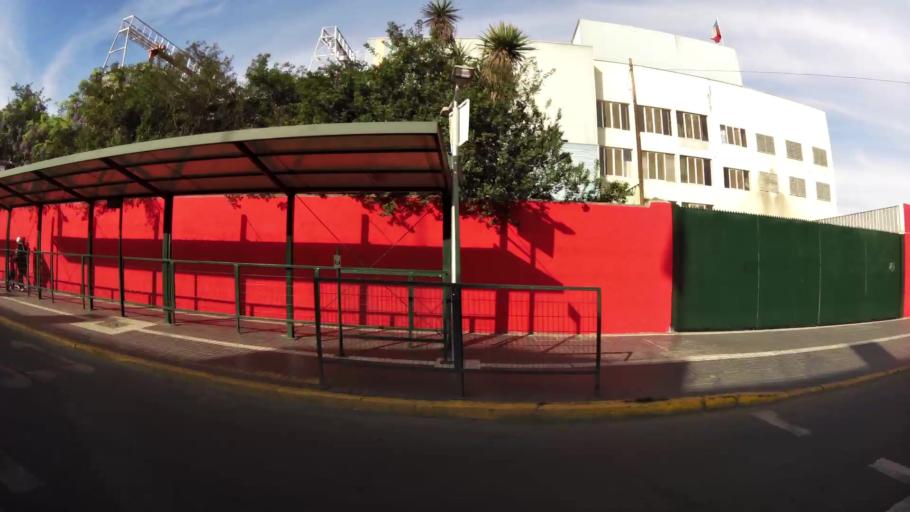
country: CL
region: Santiago Metropolitan
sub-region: Provincia de Cordillera
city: Puente Alto
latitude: -33.6118
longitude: -70.5744
